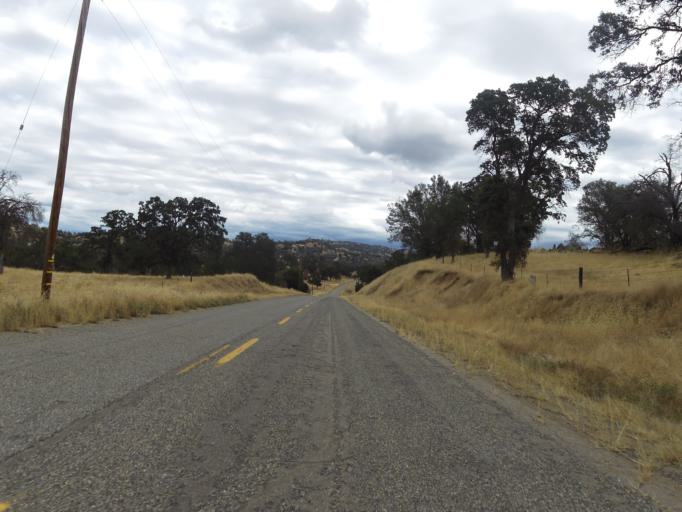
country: US
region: California
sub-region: Madera County
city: Yosemite Lakes
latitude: 37.2514
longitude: -119.8756
